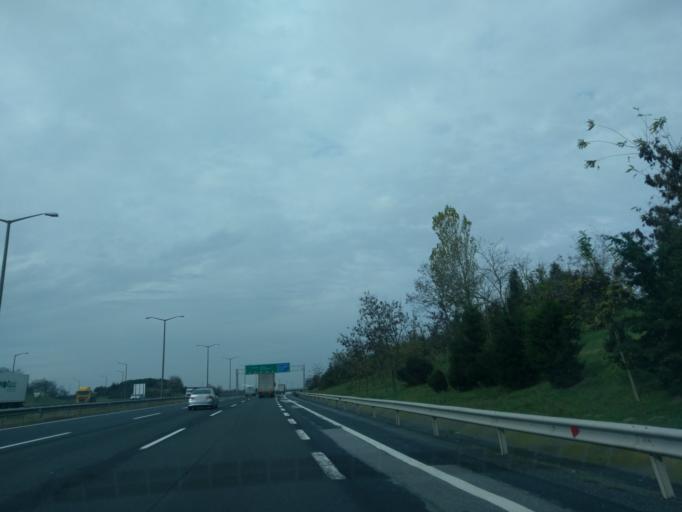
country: TR
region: Istanbul
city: Buyukcavuslu
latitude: 41.1909
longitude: 28.0910
